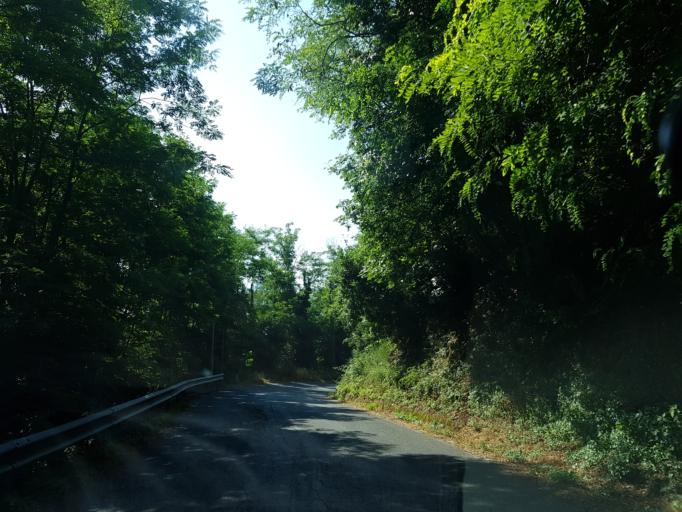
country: IT
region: Liguria
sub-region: Provincia di Genova
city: Manesseno
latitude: 44.4881
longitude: 8.9110
